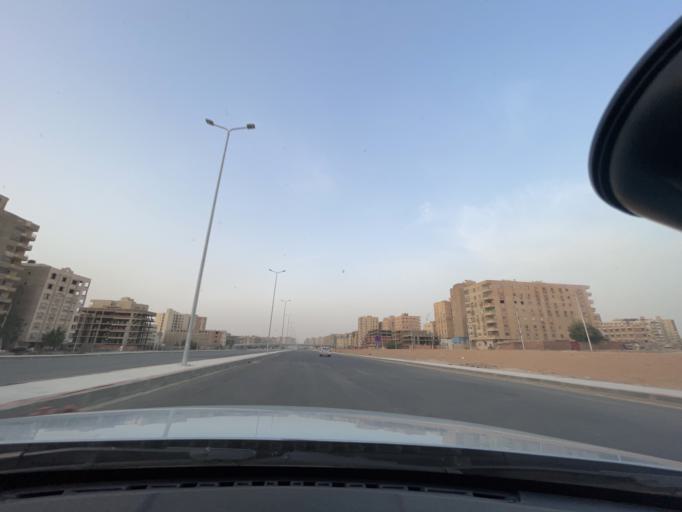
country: EG
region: Muhafazat al Qahirah
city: Cairo
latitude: 30.0539
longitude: 31.3718
